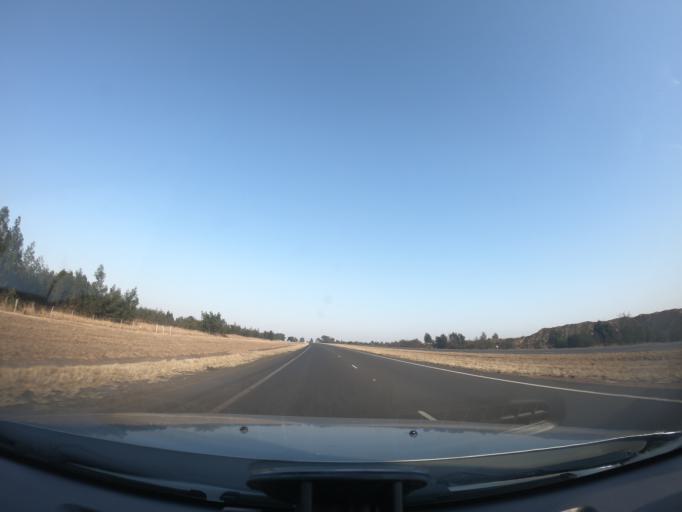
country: ZA
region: Mpumalanga
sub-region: Nkangala District Municipality
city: Middelburg
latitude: -25.8337
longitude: 29.4326
